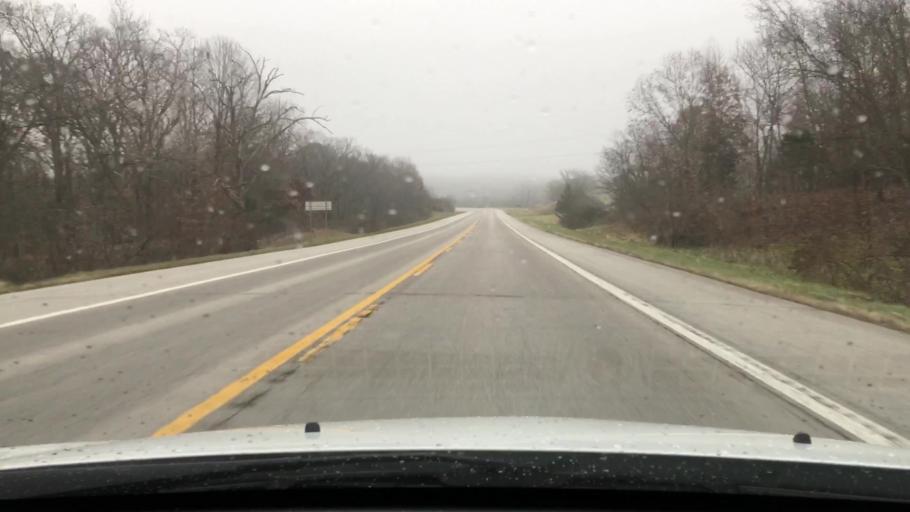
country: US
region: Missouri
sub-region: Pike County
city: Bowling Green
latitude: 39.3633
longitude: -91.1910
